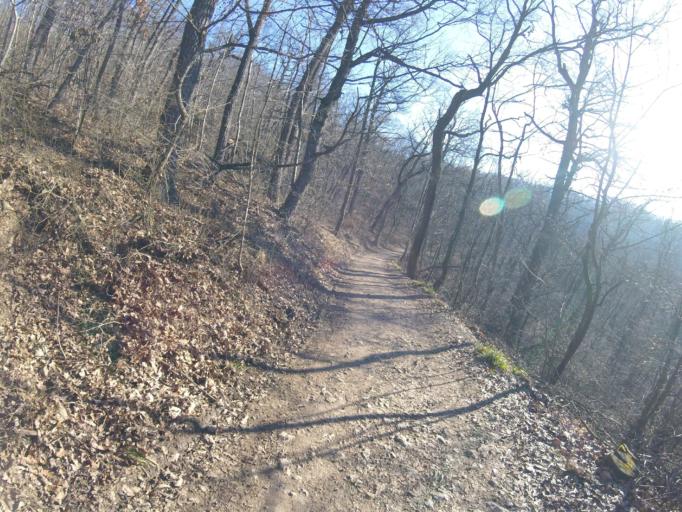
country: HU
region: Pest
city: Budakeszi
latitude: 47.5130
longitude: 18.9504
